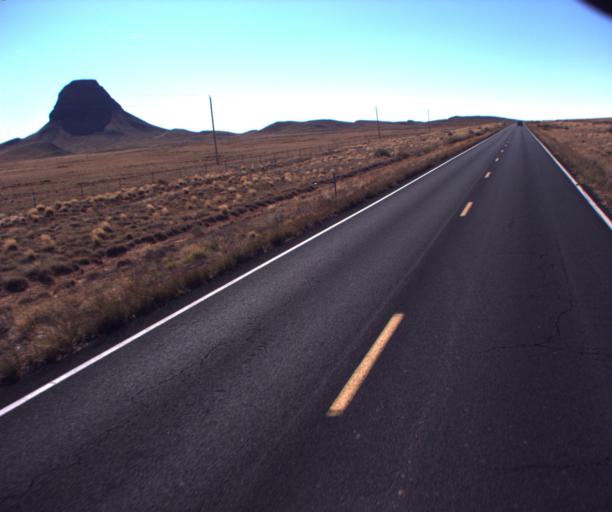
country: US
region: Arizona
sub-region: Navajo County
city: Dilkon
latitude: 35.3132
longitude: -110.4229
